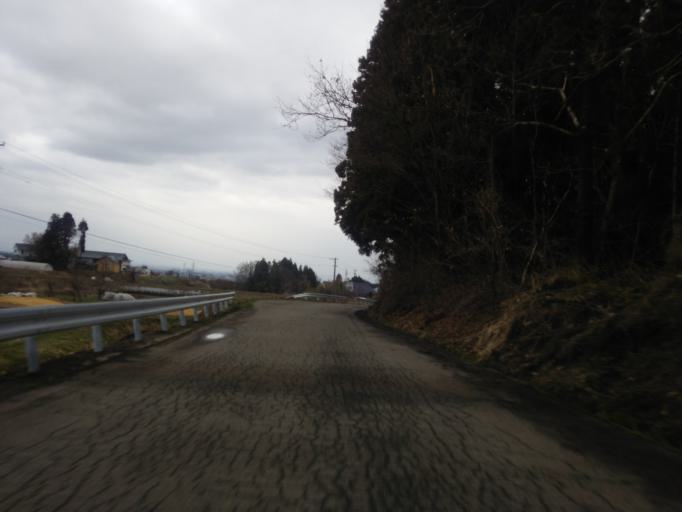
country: JP
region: Fukushima
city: Kitakata
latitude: 37.6705
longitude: 139.9162
